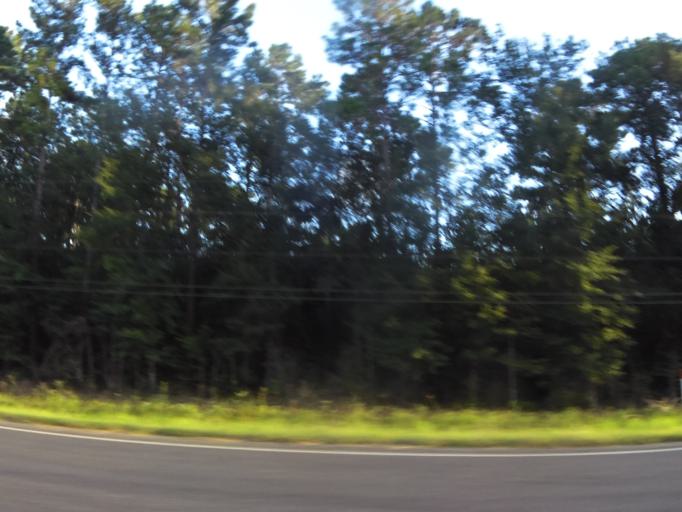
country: US
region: Georgia
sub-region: Glynn County
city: Brunswick
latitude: 31.1064
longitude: -81.6454
